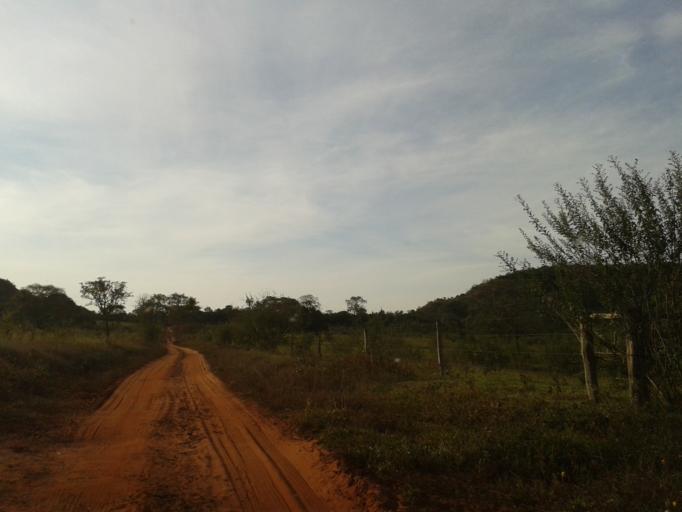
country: BR
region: Minas Gerais
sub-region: Campina Verde
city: Campina Verde
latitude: -19.5014
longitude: -49.6048
